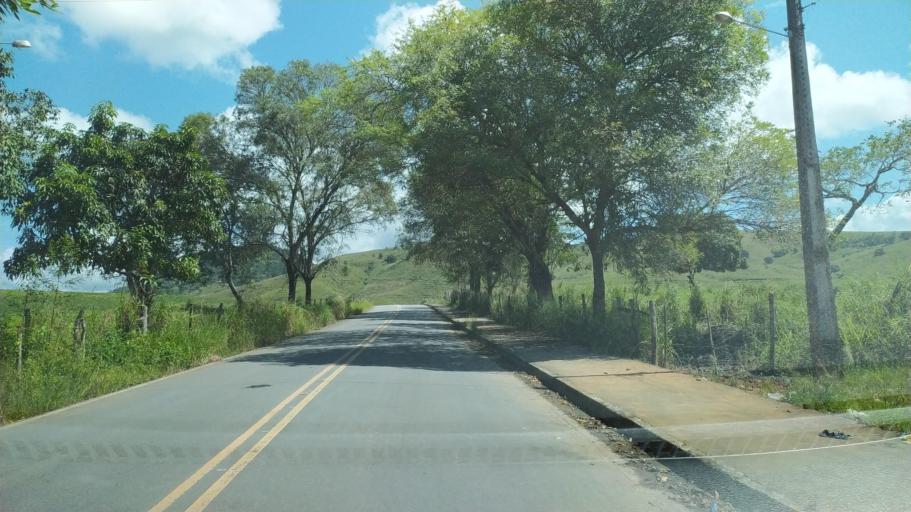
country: BR
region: Alagoas
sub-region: Uniao Dos Palmares
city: Uniao dos Palmares
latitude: -9.1627
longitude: -36.0492
